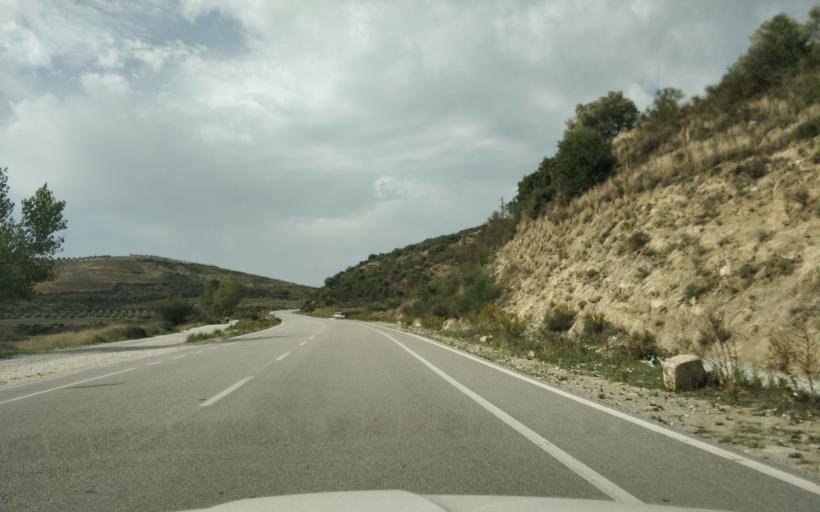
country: AL
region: Gjirokaster
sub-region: Rrethi i Tepelenes
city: Krahes
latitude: 40.3919
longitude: 19.8757
